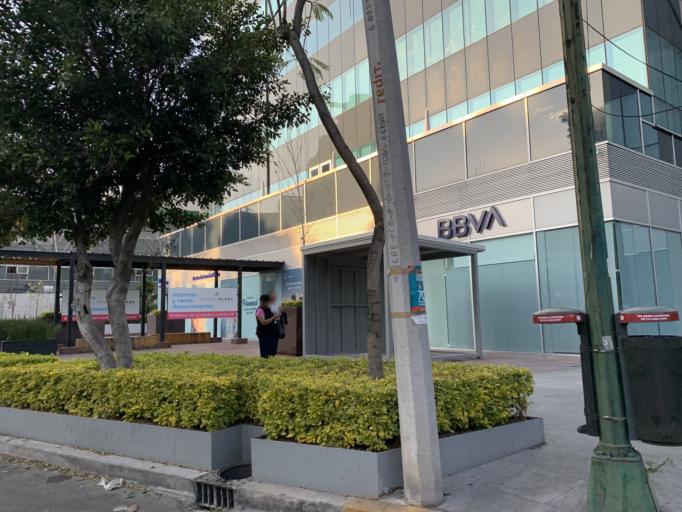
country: MX
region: Mexico City
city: Miguel Hidalgo
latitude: 19.4385
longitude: -99.1781
